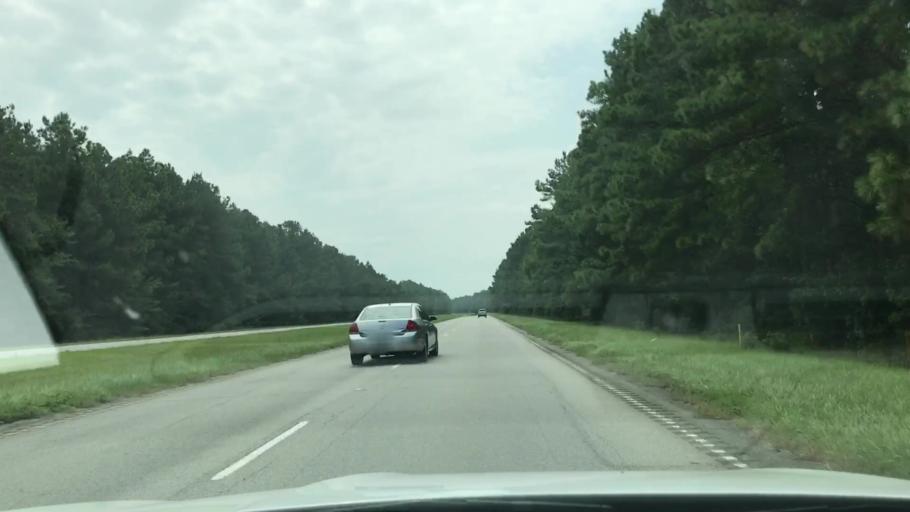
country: US
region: South Carolina
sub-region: Charleston County
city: Awendaw
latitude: 32.9775
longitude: -79.6660
